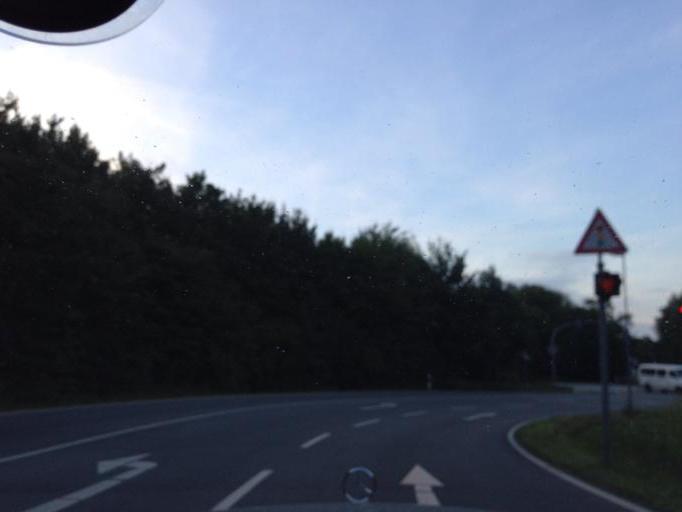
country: DE
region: Schleswig-Holstein
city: Bargteheide
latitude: 53.7224
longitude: 10.2653
